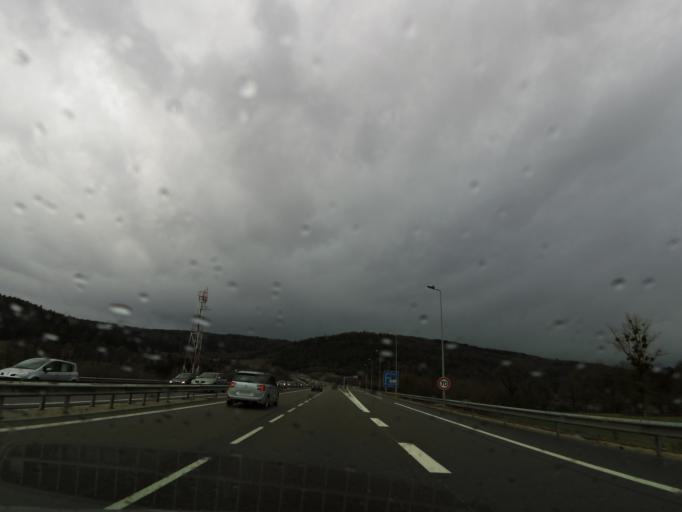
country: FR
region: Rhone-Alpes
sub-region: Departement de l'Ain
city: Saint-Martin-du-Frene
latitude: 46.1326
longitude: 5.5450
